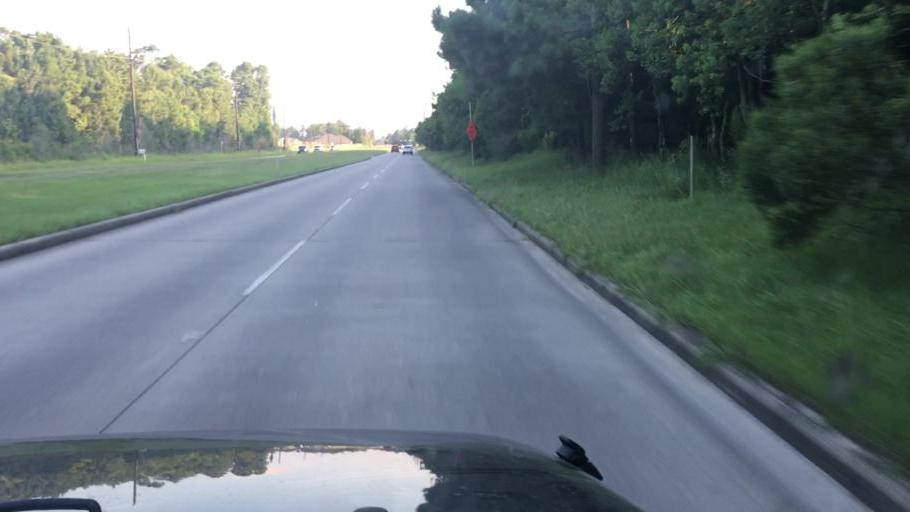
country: US
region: Texas
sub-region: Harris County
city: Atascocita
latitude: 29.9510
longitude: -95.1745
